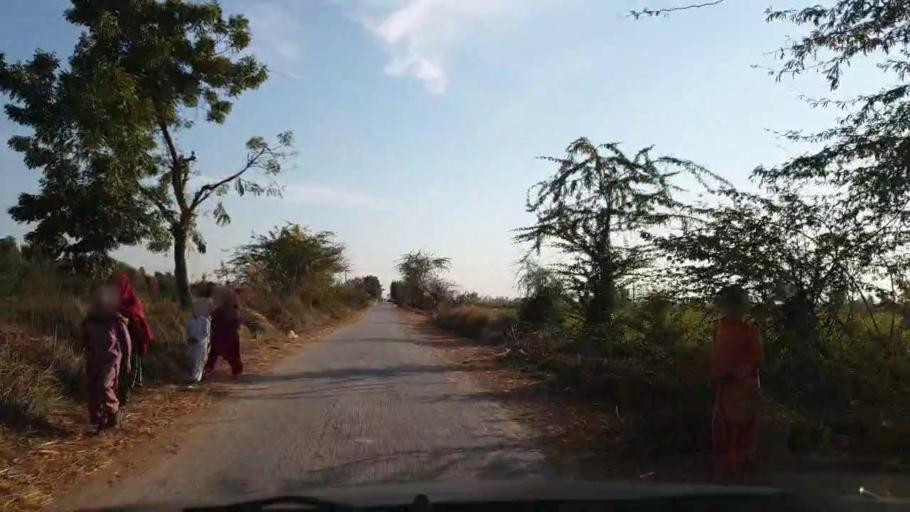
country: PK
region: Sindh
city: Khadro
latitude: 26.1870
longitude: 68.7498
